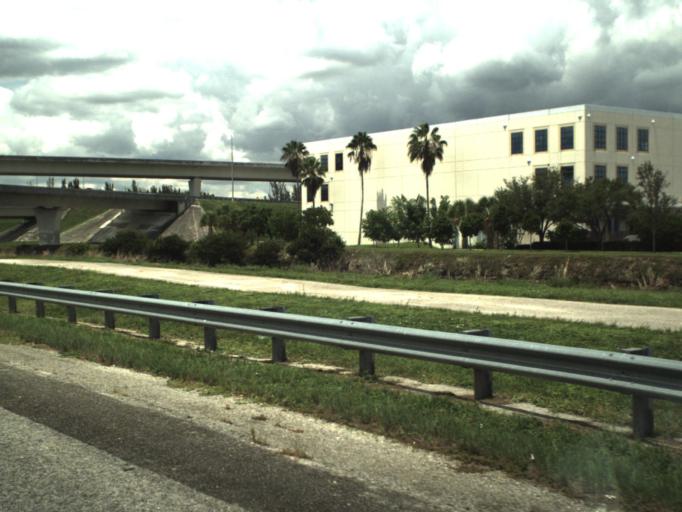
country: US
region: Florida
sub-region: Broward County
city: Weston
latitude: 26.1217
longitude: -80.3417
